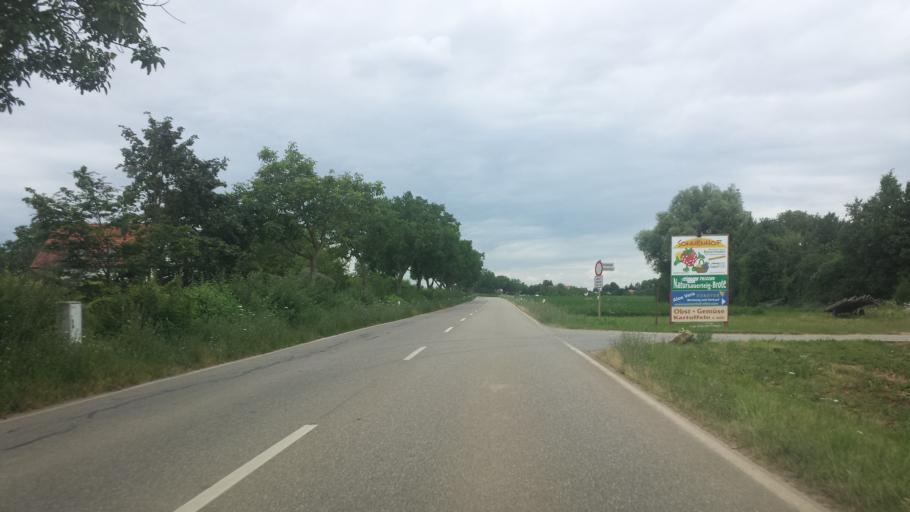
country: DE
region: Rheinland-Pfalz
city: Meckenheim
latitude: 49.3921
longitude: 8.2450
